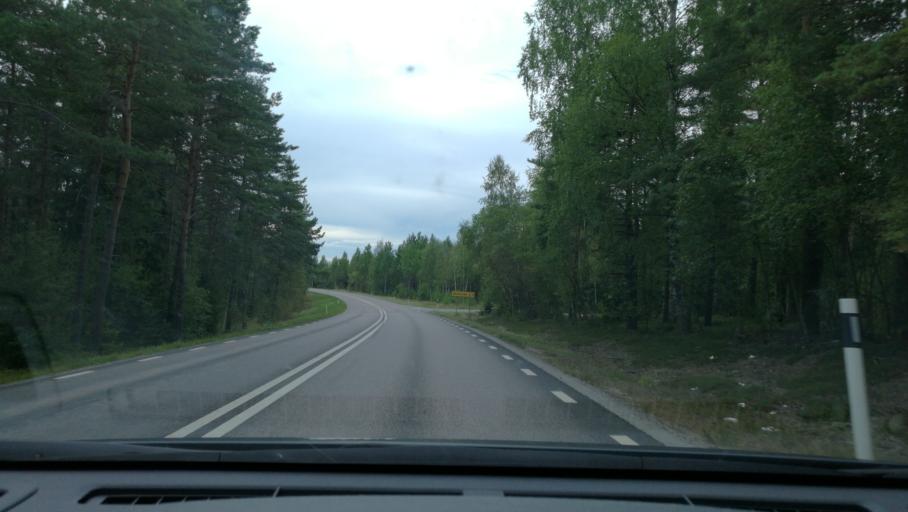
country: SE
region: Soedermanland
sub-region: Katrineholms Kommun
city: Katrineholm
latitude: 59.1351
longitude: 16.1374
